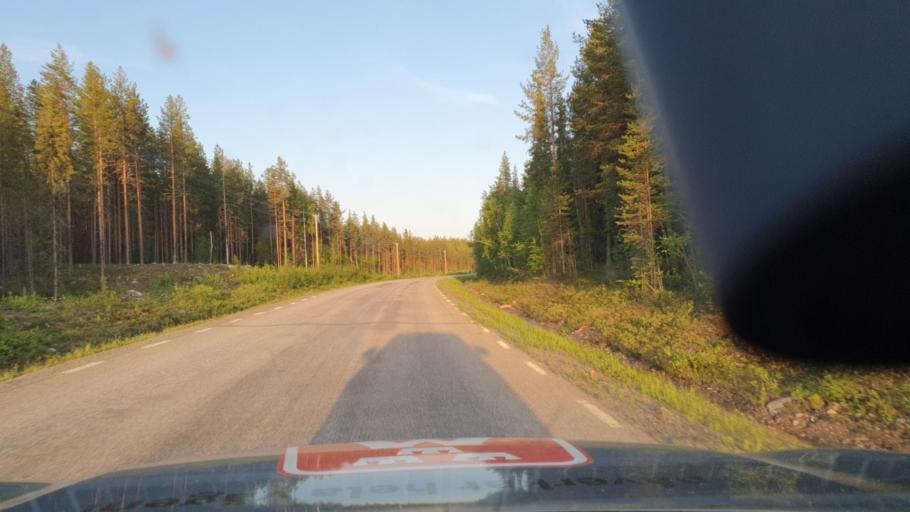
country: SE
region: Norrbotten
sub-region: Bodens Kommun
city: Boden
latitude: 66.0130
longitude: 21.8374
